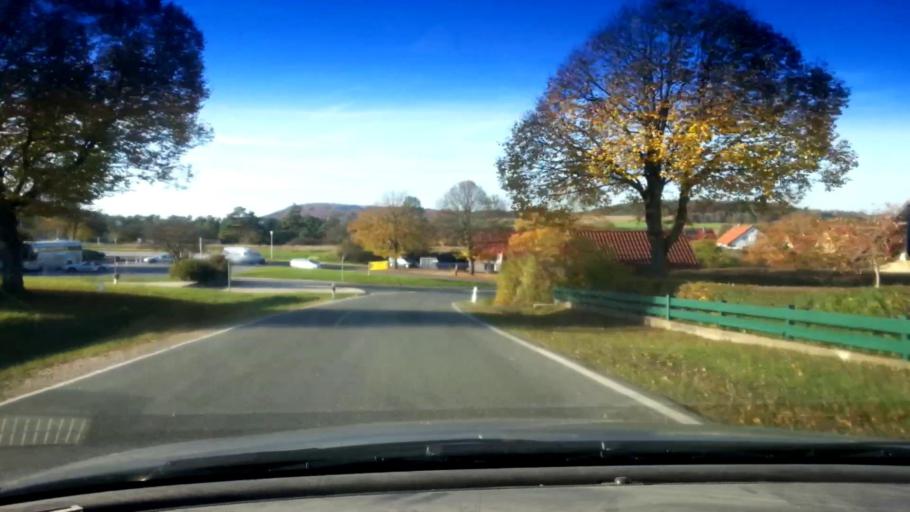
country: DE
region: Bavaria
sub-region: Upper Franconia
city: Heiligenstadt
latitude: 49.8628
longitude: 11.1641
